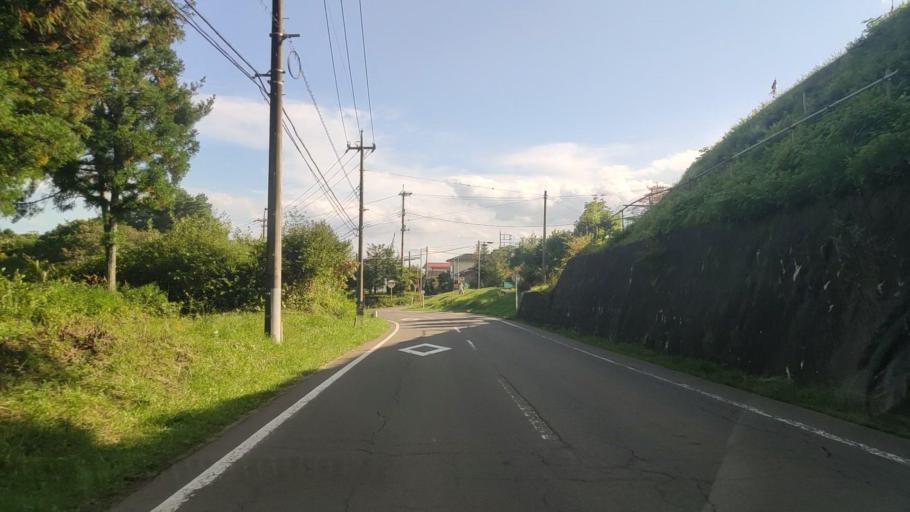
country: JP
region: Nagano
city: Suzaka
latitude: 36.5648
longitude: 138.5541
